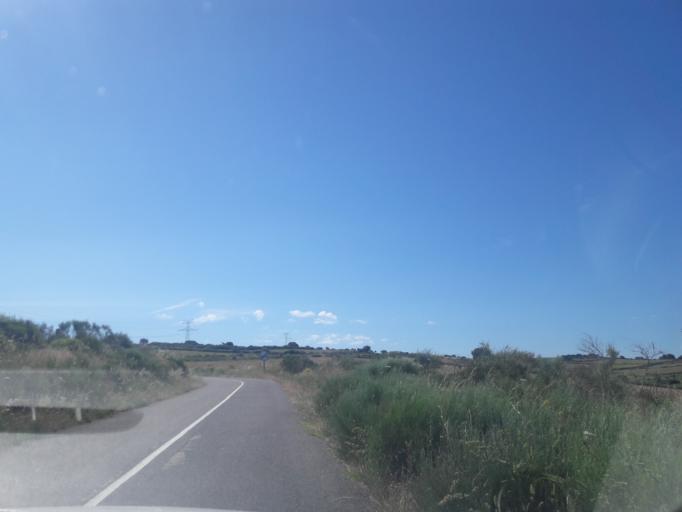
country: ES
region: Castille and Leon
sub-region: Provincia de Salamanca
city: Saucelle
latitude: 40.9932
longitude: -6.7334
